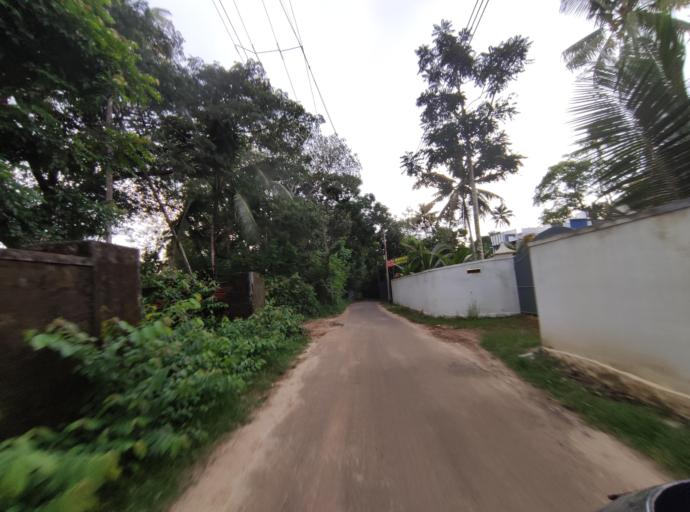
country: IN
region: Kerala
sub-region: Alappuzha
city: Shertallai
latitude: 9.6677
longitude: 76.3378
